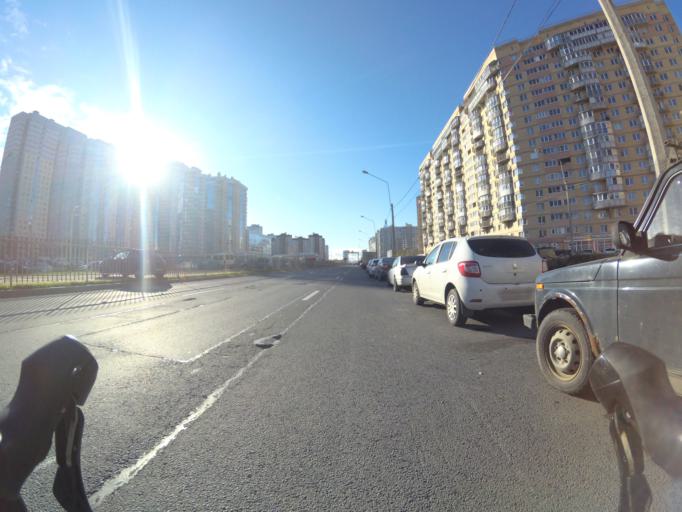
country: RU
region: Leningrad
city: Untolovo
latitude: 60.0042
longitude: 30.2108
